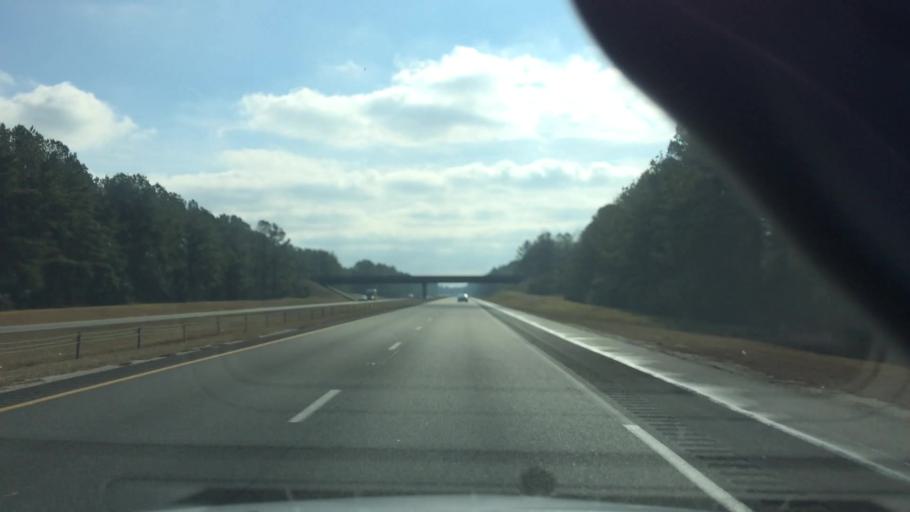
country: US
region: North Carolina
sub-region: Pender County
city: Rocky Point
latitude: 34.4817
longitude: -77.8787
